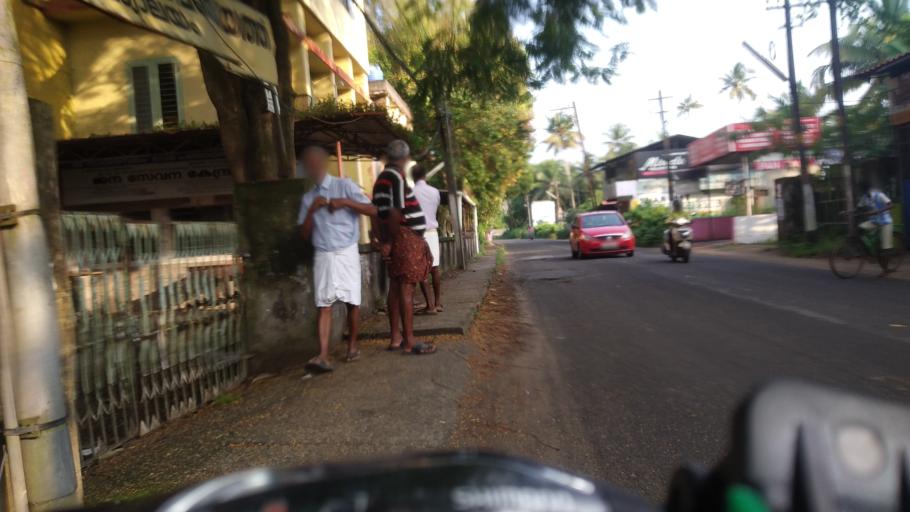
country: IN
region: Kerala
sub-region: Ernakulam
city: Elur
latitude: 10.0602
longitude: 76.2140
